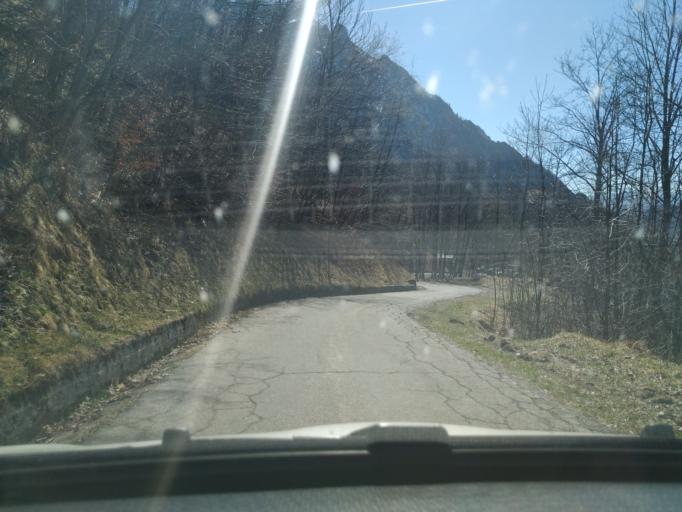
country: IT
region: Piedmont
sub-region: Provincia di Vercelli
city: Rimella
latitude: 45.9084
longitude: 8.1850
